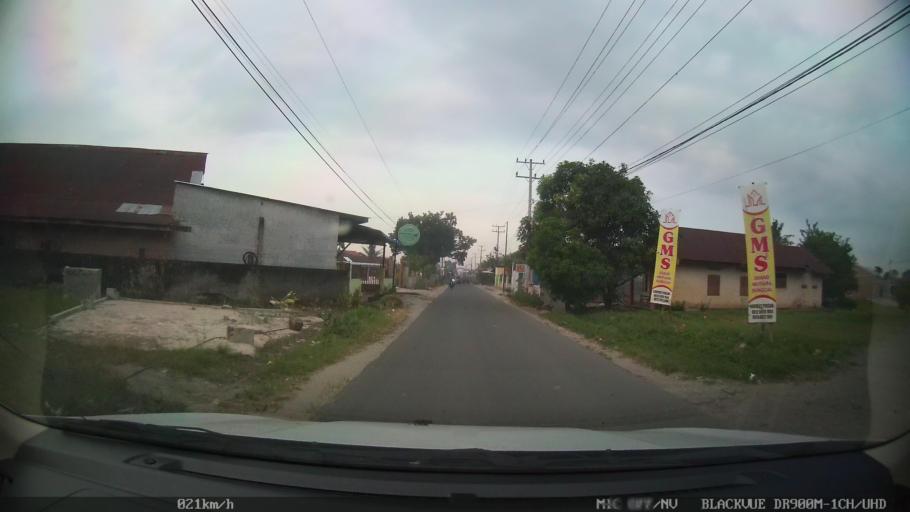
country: ID
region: North Sumatra
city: Sunggal
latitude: 3.5632
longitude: 98.5764
